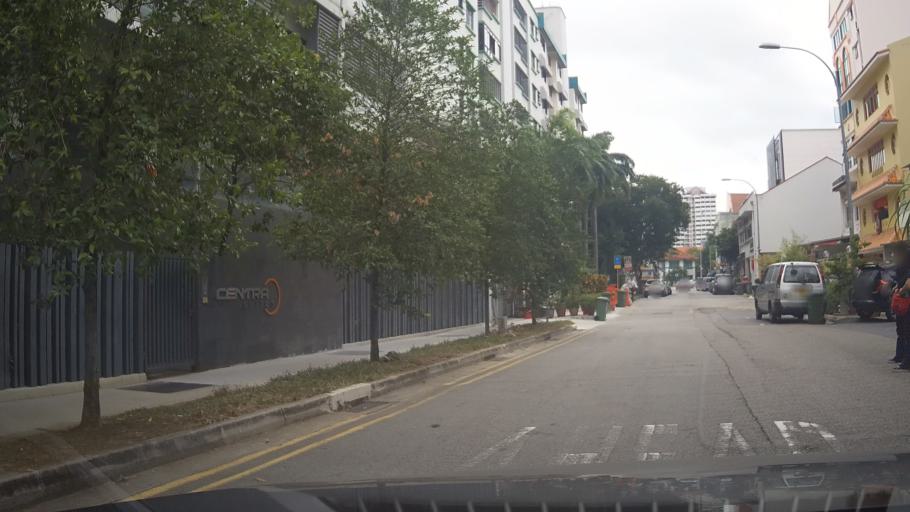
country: SG
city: Singapore
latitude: 1.3148
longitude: 103.8831
